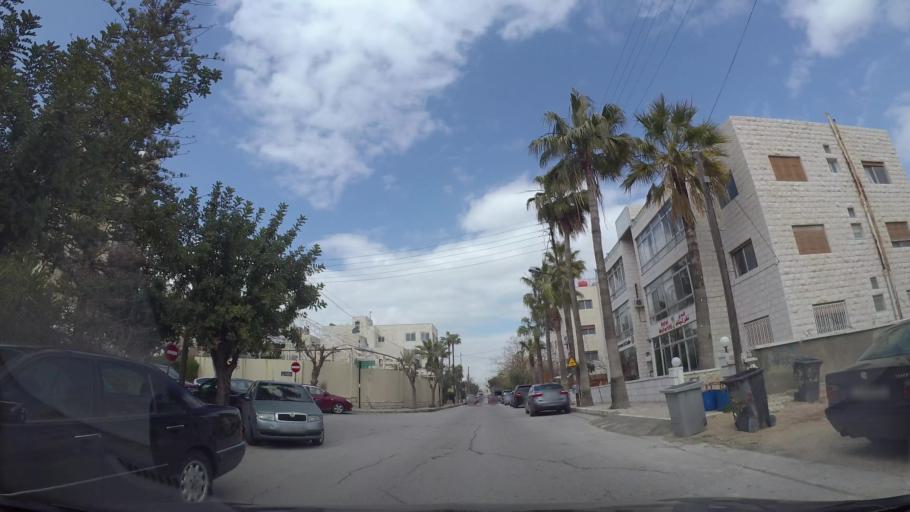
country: JO
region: Amman
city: Amman
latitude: 31.9732
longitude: 35.8988
